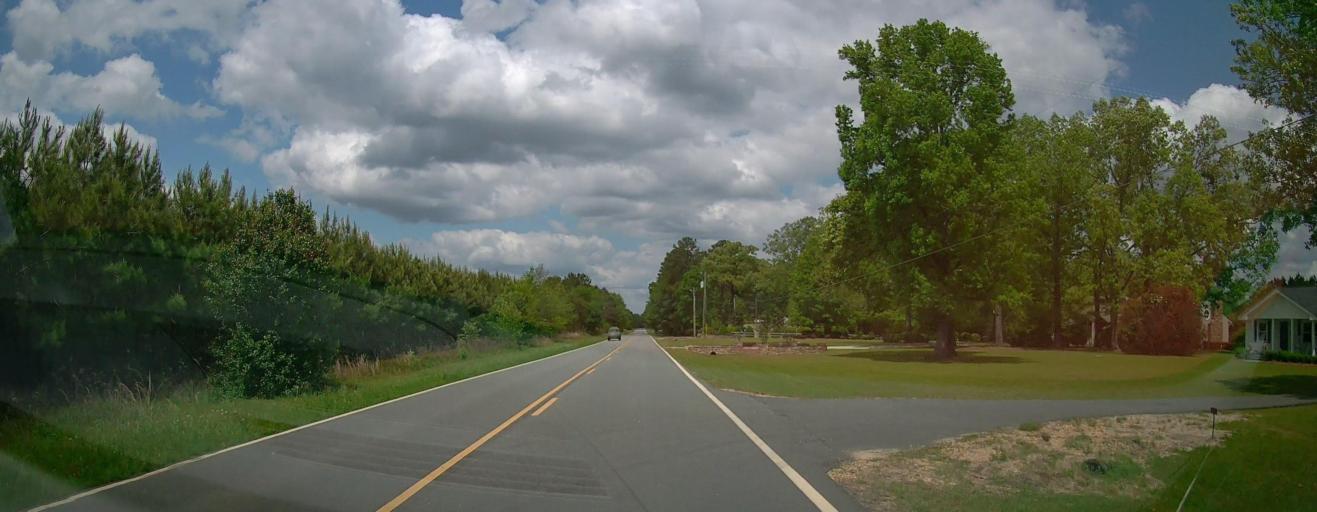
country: US
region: Georgia
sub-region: Laurens County
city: Dublin
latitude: 32.5925
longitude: -82.9498
